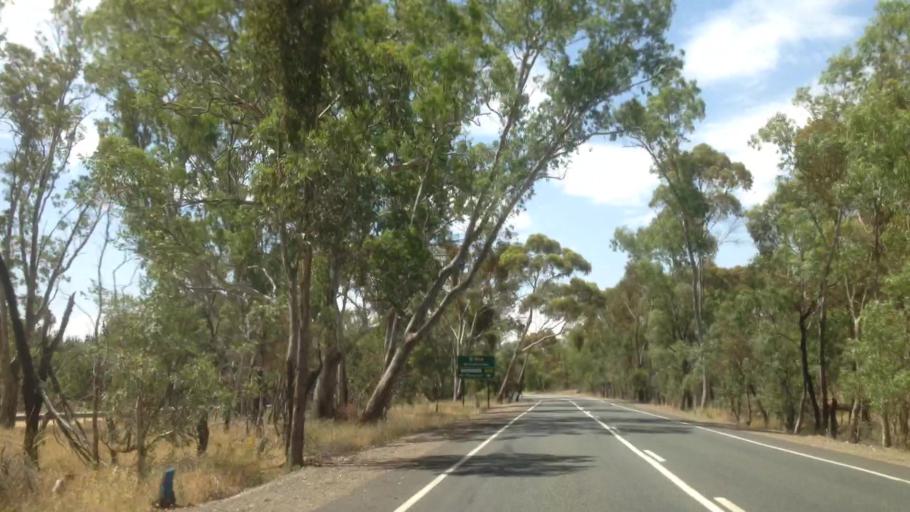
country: AU
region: South Australia
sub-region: Adelaide Hills
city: Birdwood
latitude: -34.7357
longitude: 138.9620
